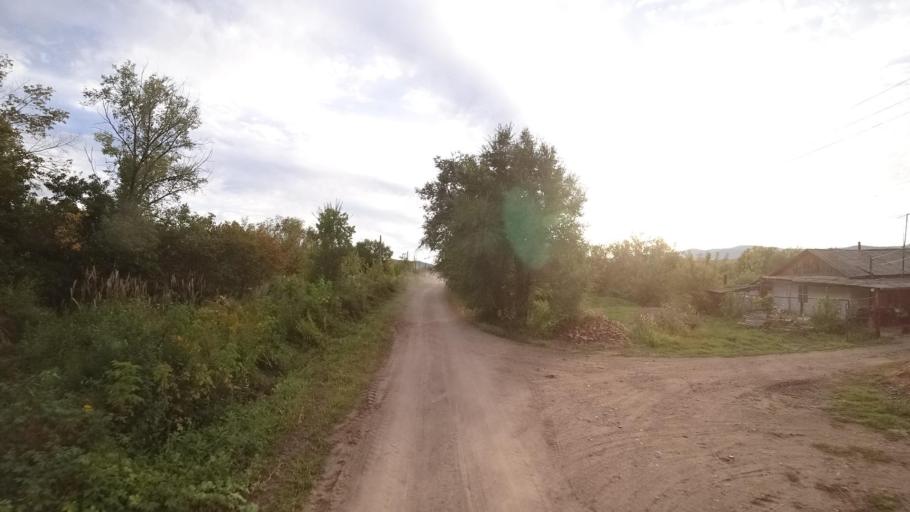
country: RU
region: Primorskiy
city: Yakovlevka
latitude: 44.4227
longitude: 133.4568
